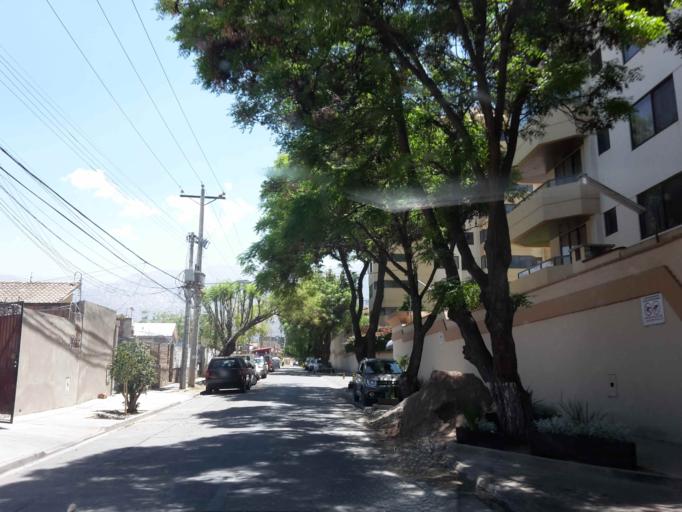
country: BO
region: Cochabamba
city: Cochabamba
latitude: -17.3746
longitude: -66.1848
